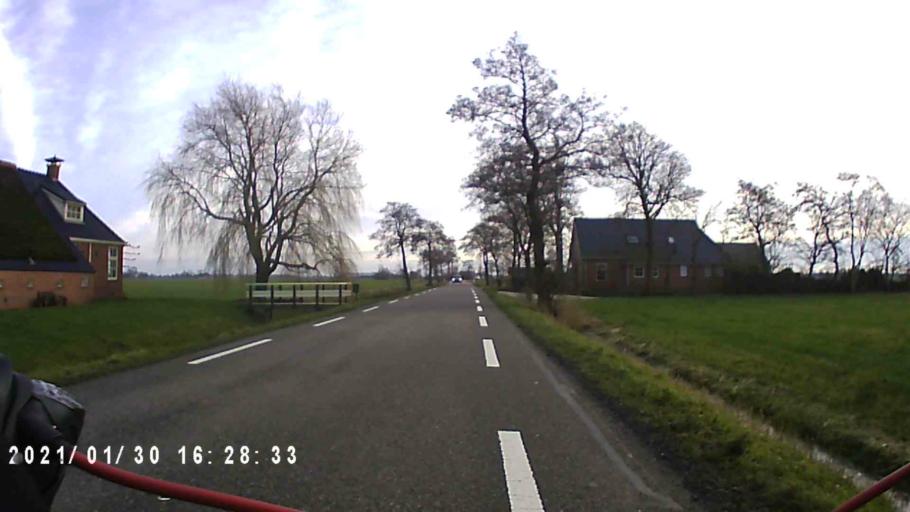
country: NL
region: Groningen
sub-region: Gemeente Zuidhorn
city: Zuidhorn
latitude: 53.2251
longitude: 6.3831
